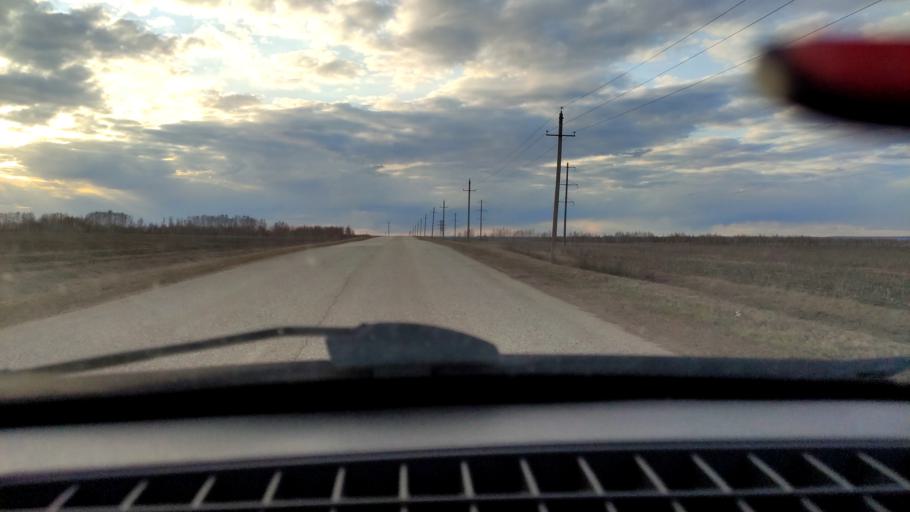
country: RU
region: Bashkortostan
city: Tolbazy
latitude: 54.0049
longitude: 55.7588
